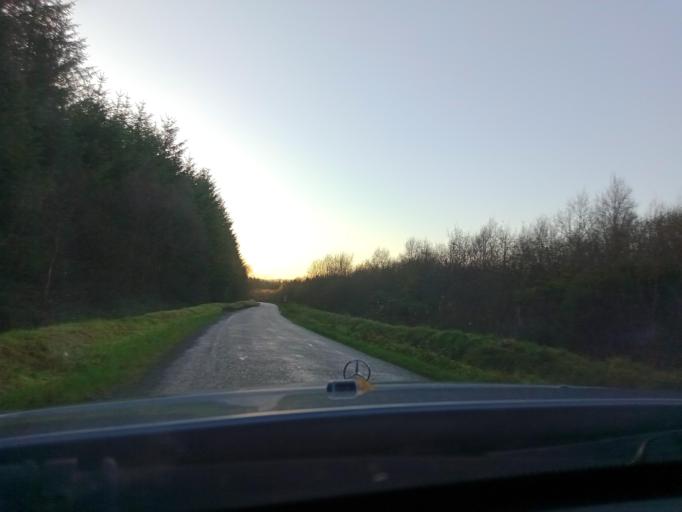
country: IE
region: Munster
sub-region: Waterford
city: Waterford
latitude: 52.3694
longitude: -7.1084
